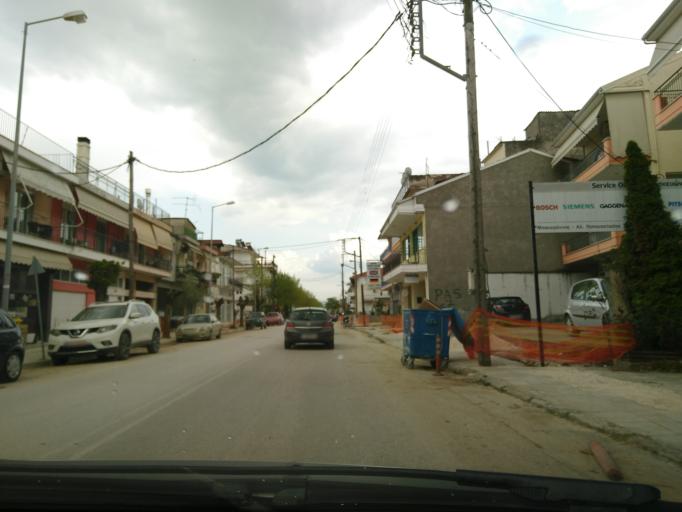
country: GR
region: Epirus
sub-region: Nomos Ioanninon
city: Anatoli
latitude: 39.6480
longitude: 20.8614
